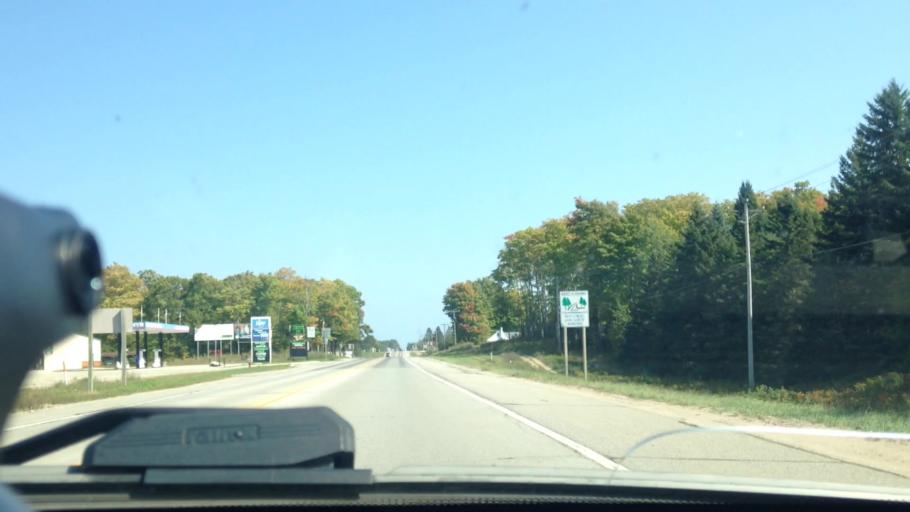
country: US
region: Michigan
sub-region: Luce County
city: Newberry
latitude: 46.3034
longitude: -85.5069
